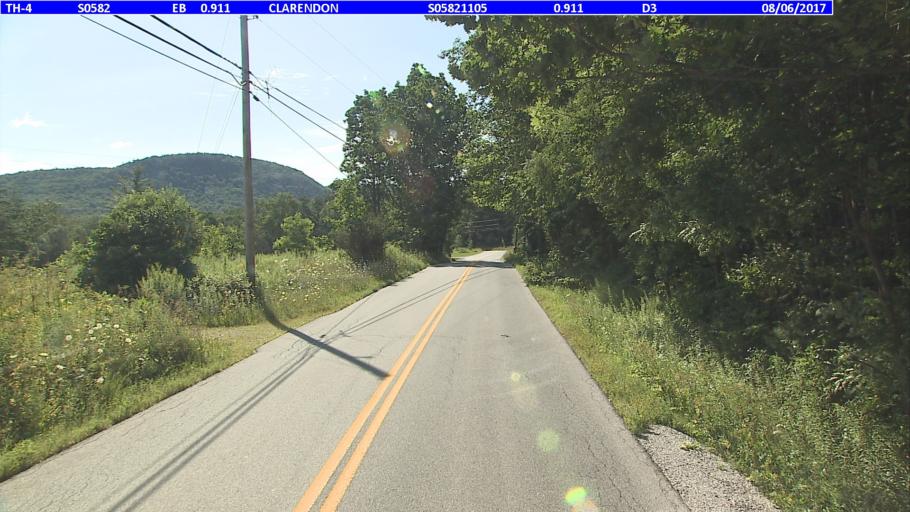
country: US
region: Vermont
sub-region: Rutland County
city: Rutland
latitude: 43.5671
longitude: -72.9466
